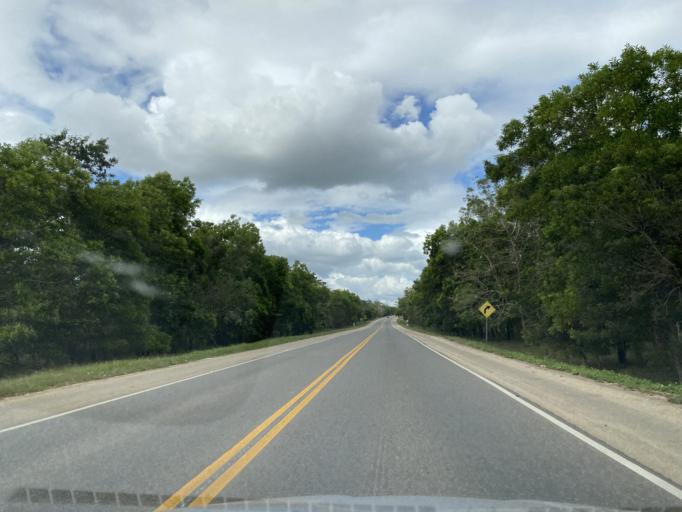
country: DO
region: Santo Domingo
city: Guerra
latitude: 18.5485
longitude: -69.7623
